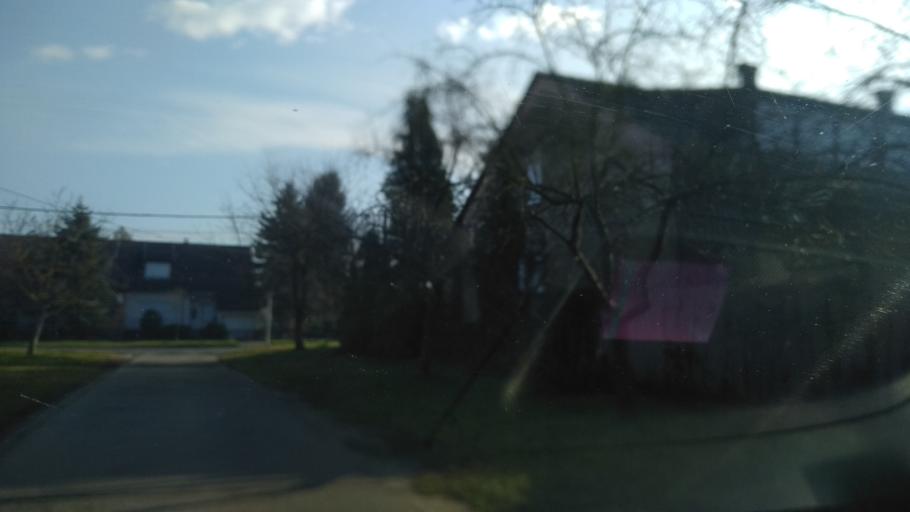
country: HU
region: Somogy
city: Barcs
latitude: 45.9641
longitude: 17.4708
